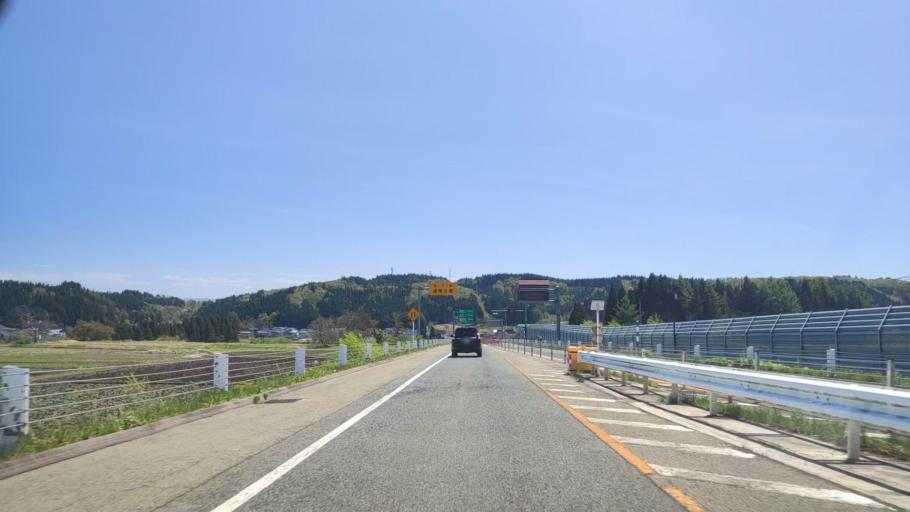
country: JP
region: Yamagata
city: Shinjo
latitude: 38.6983
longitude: 140.3107
